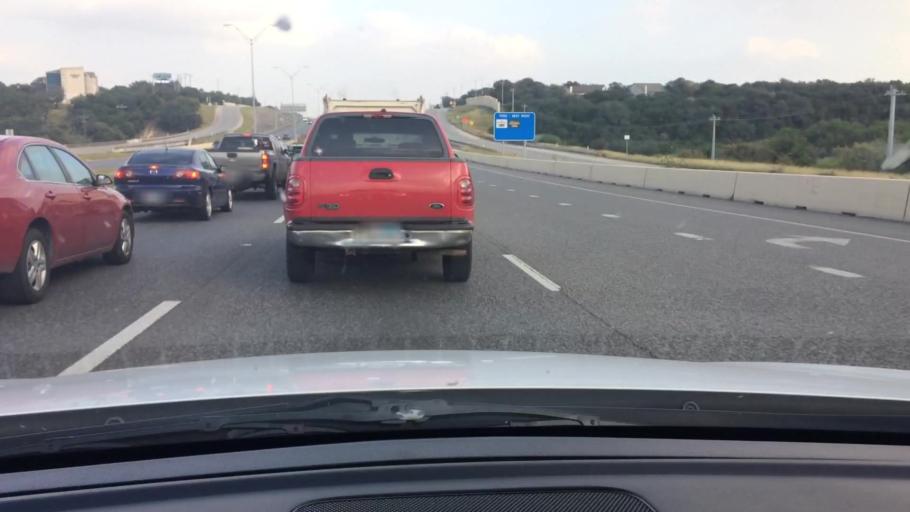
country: US
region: Texas
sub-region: Bexar County
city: Hollywood Park
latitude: 29.6046
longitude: -98.4529
